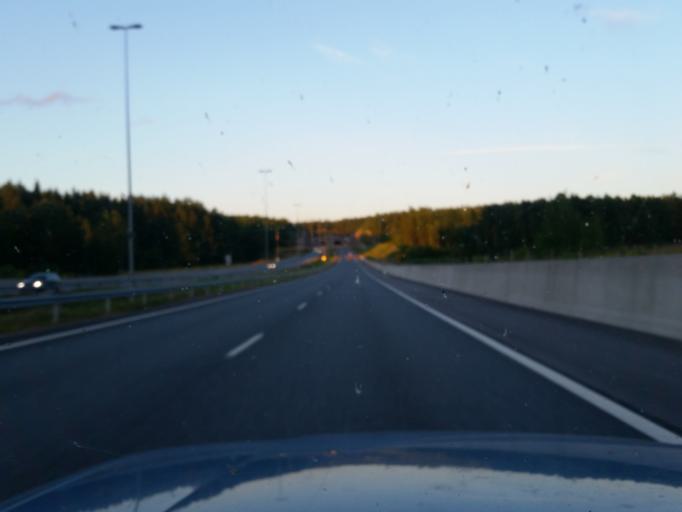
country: FI
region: Varsinais-Suomi
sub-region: Salo
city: Muurla
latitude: 60.3748
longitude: 23.3433
